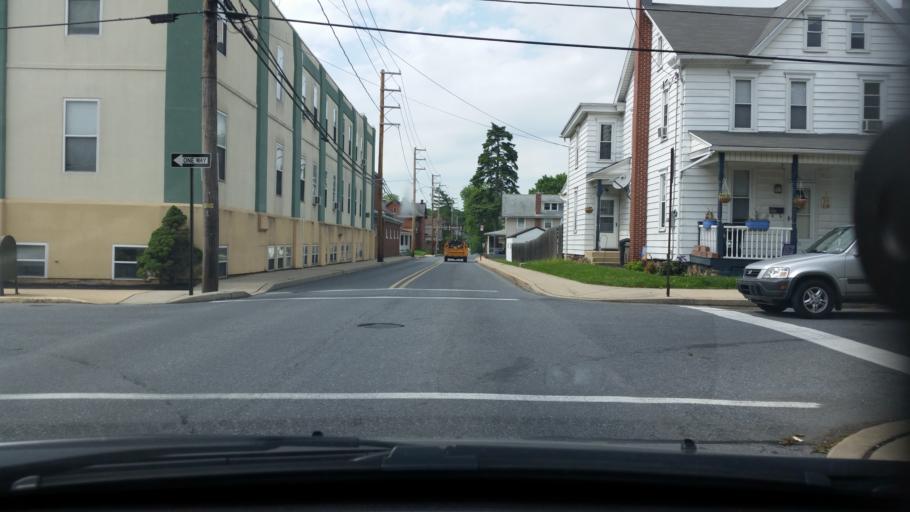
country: US
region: Pennsylvania
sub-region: Lancaster County
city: Elizabethtown
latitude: 40.1516
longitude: -76.6015
